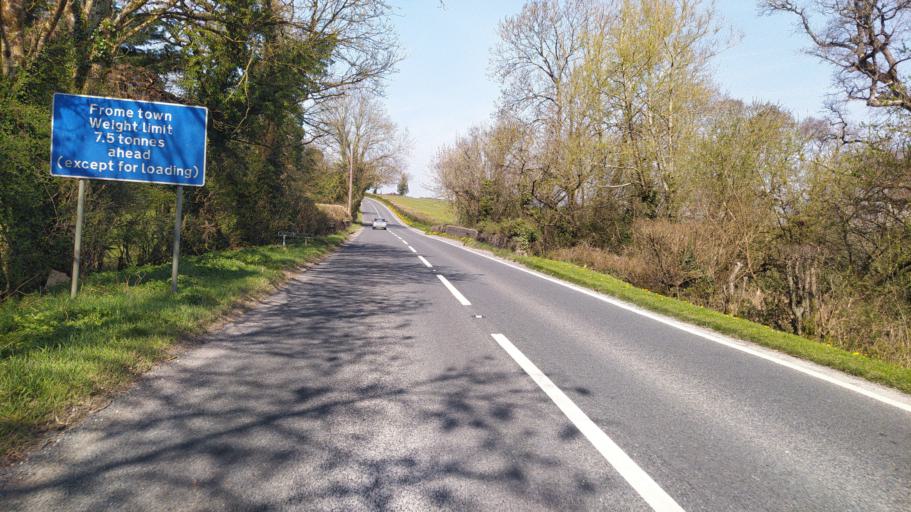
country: GB
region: England
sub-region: Wiltshire
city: Corsley
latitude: 51.2193
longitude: -2.2852
